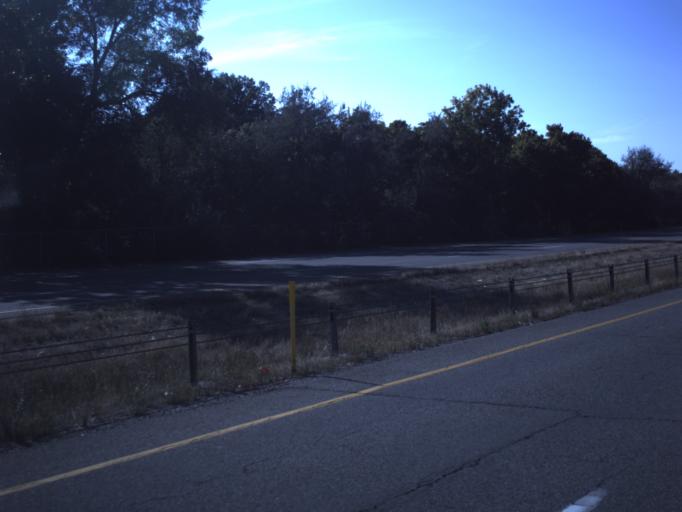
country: US
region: Utah
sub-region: Salt Lake County
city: Millcreek
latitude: 40.6636
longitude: -111.8594
